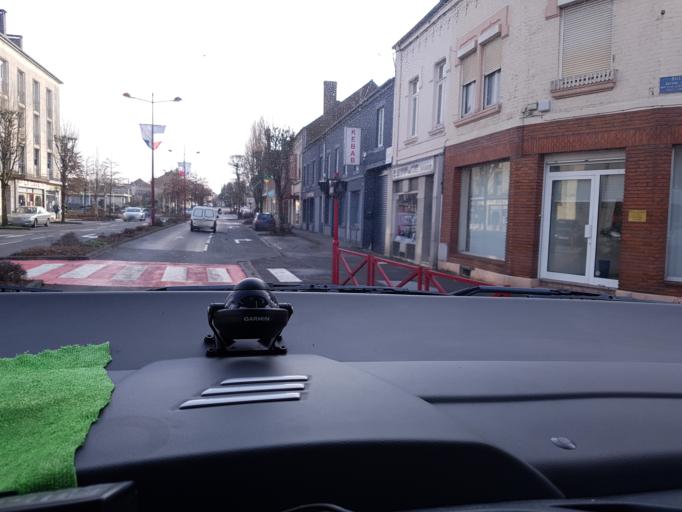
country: FR
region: Picardie
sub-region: Departement de l'Aisne
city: Hirson
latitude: 49.9180
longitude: 4.0854
